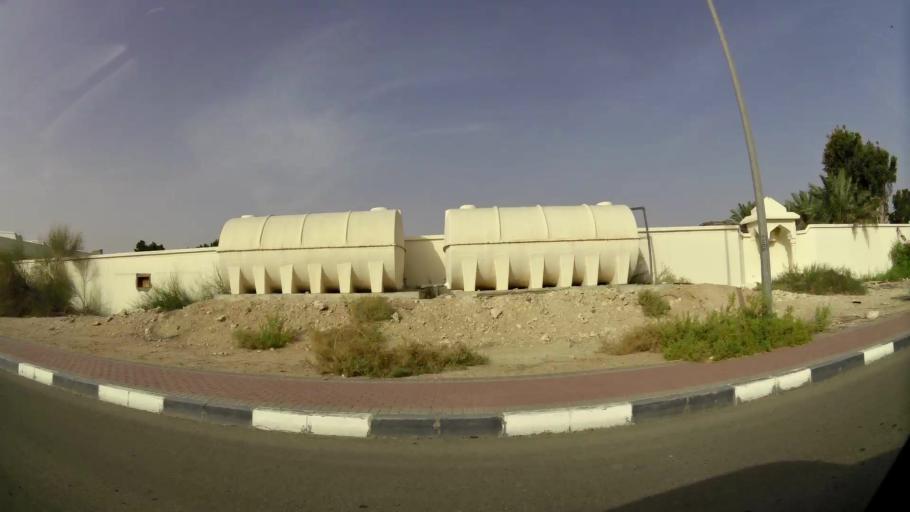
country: AE
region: Abu Dhabi
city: Al Ain
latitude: 24.1249
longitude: 55.6853
